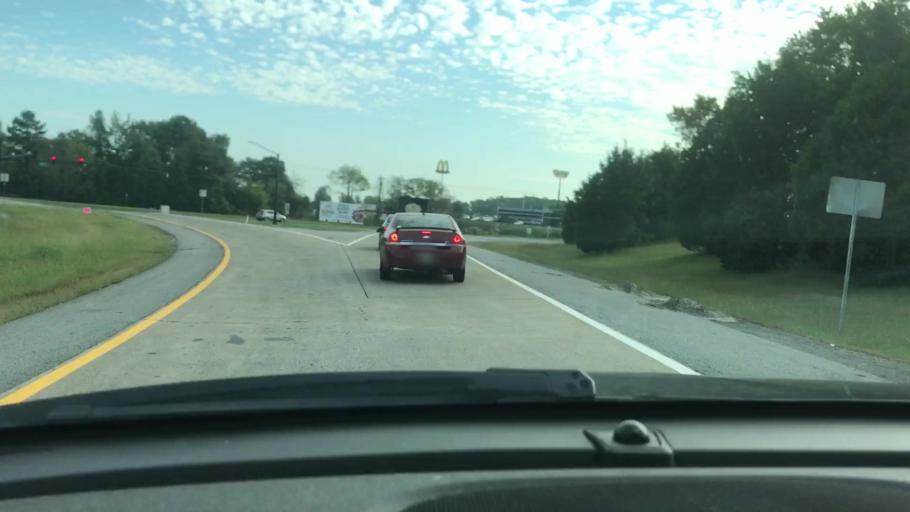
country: US
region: Tennessee
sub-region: Sumner County
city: White House
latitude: 36.4679
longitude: -86.6807
